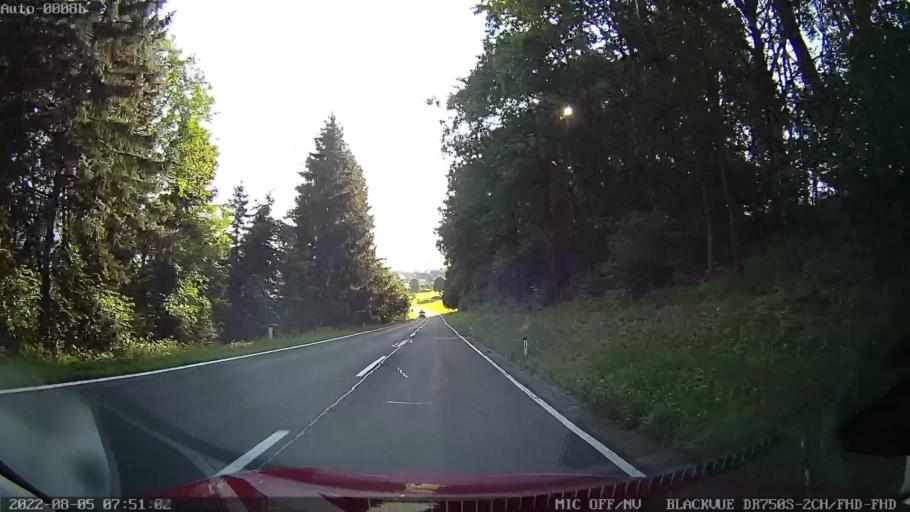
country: AT
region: Carinthia
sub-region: Politischer Bezirk Villach Land
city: Arnoldstein
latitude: 46.5483
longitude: 13.7822
